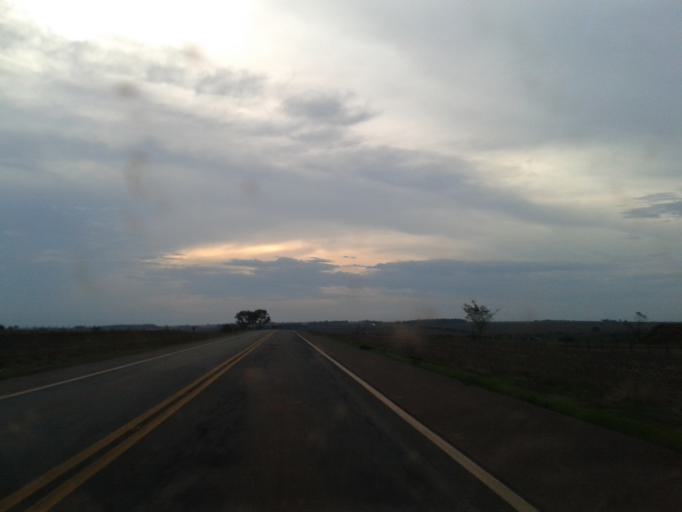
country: BR
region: Goias
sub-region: Santa Helena De Goias
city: Santa Helena de Goias
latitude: -17.8814
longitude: -50.6981
